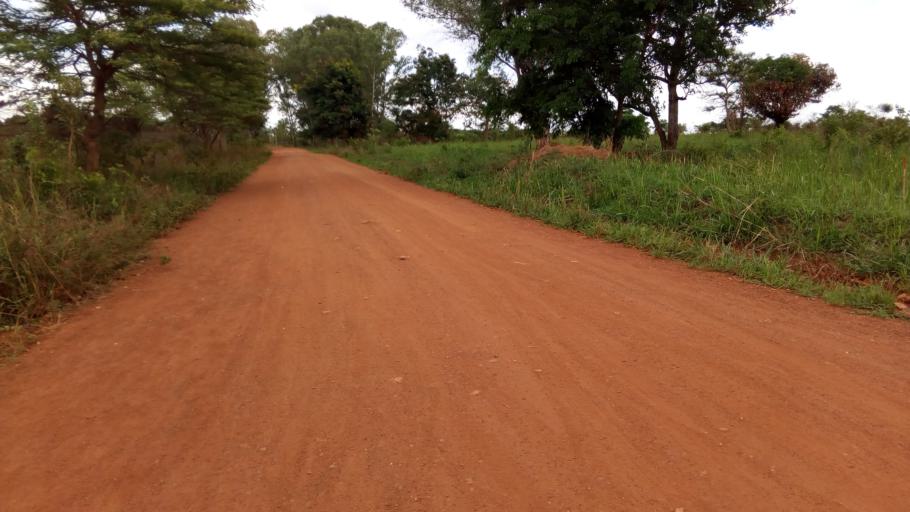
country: UG
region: Northern Region
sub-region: Gulu District
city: Gulu
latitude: 2.7871
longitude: 32.3486
